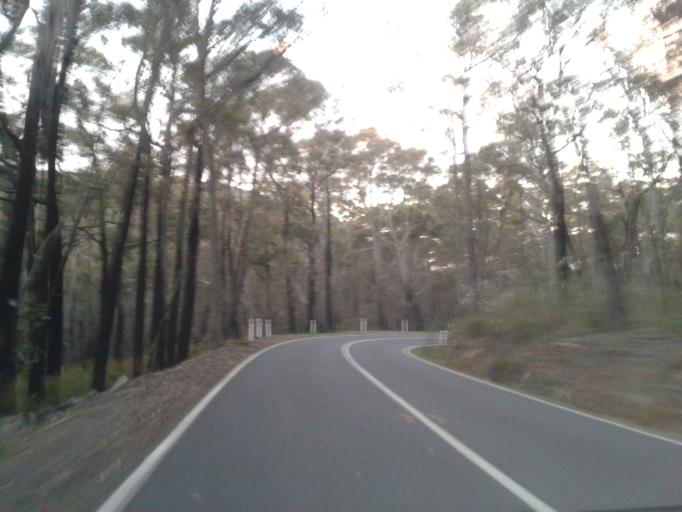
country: AU
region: Victoria
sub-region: Northern Grampians
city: Stawell
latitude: -37.1544
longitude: 142.4873
